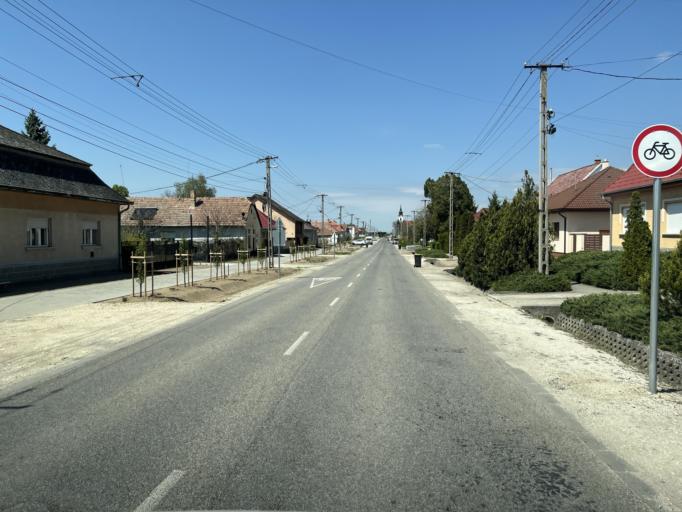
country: HU
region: Pest
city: Ujhartyan
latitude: 47.2180
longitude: 19.3878
